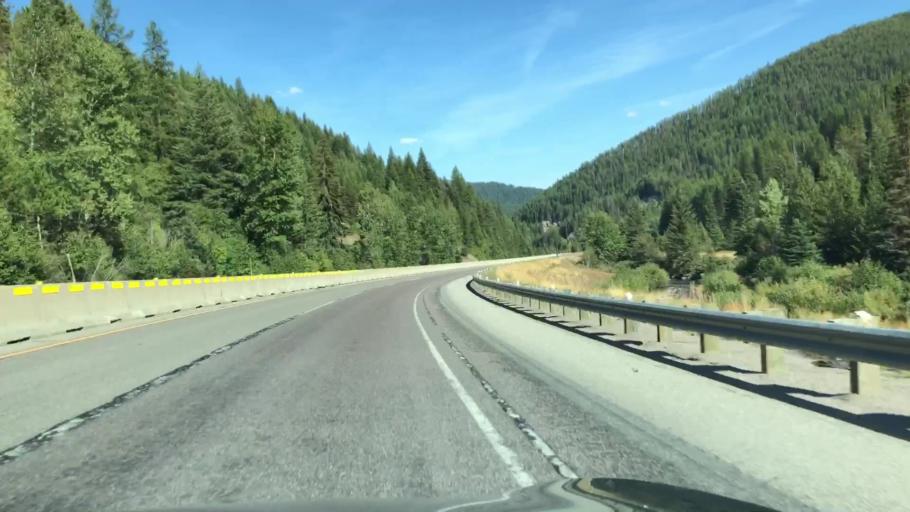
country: US
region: Montana
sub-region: Sanders County
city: Thompson Falls
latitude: 47.4178
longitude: -115.5568
